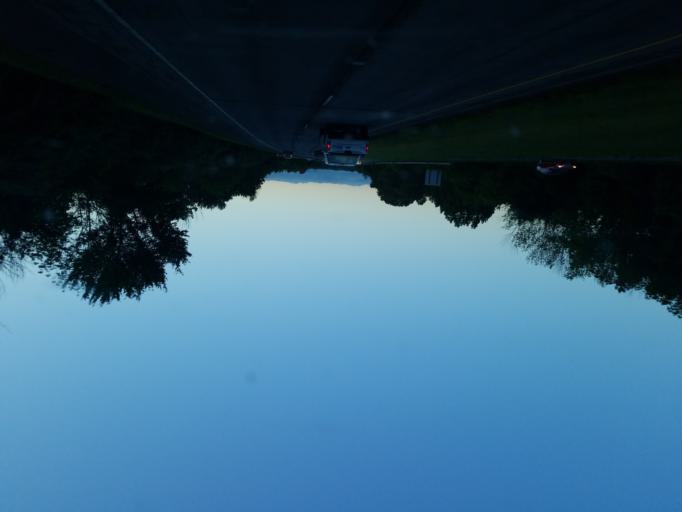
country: US
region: Ohio
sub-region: Summit County
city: Norton
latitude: 41.0096
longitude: -81.6622
